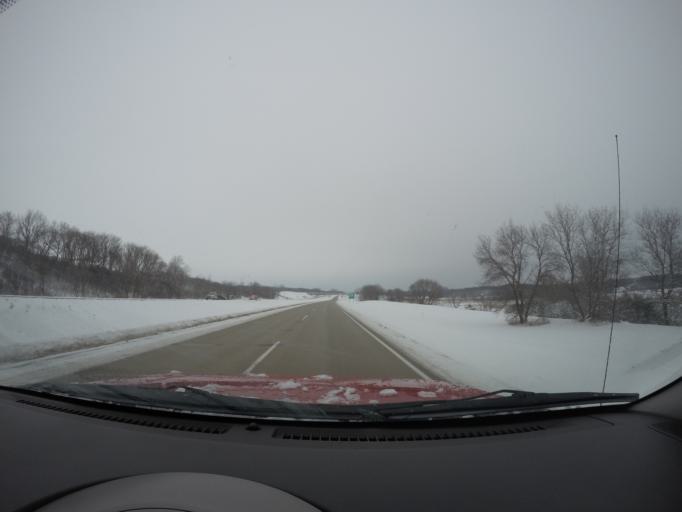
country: US
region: Minnesota
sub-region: Olmsted County
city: Rochester
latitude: 43.9561
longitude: -92.3714
